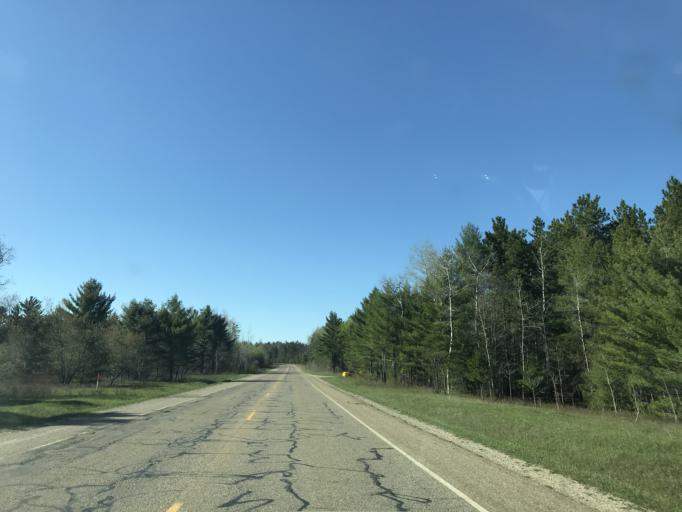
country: US
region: Michigan
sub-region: Crawford County
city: Grayling
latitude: 44.7159
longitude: -84.7438
